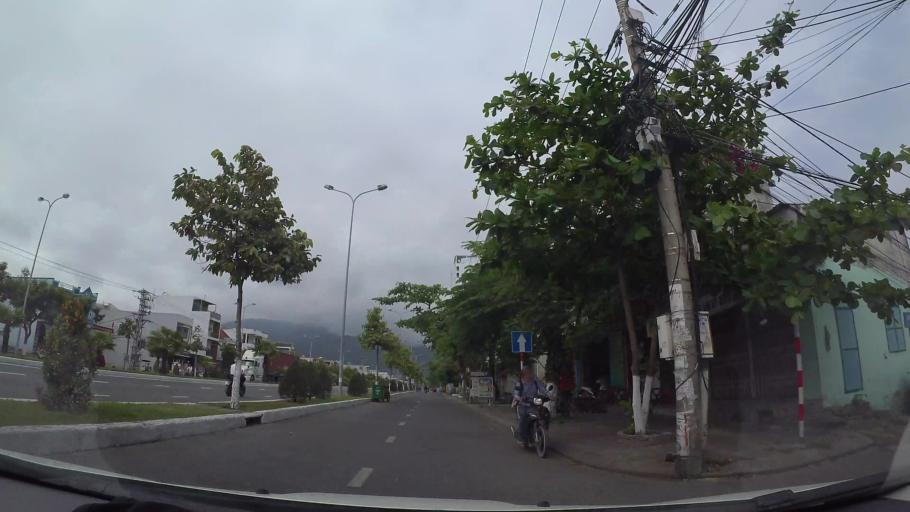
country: VN
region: Da Nang
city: Da Nang
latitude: 16.0943
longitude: 108.2446
